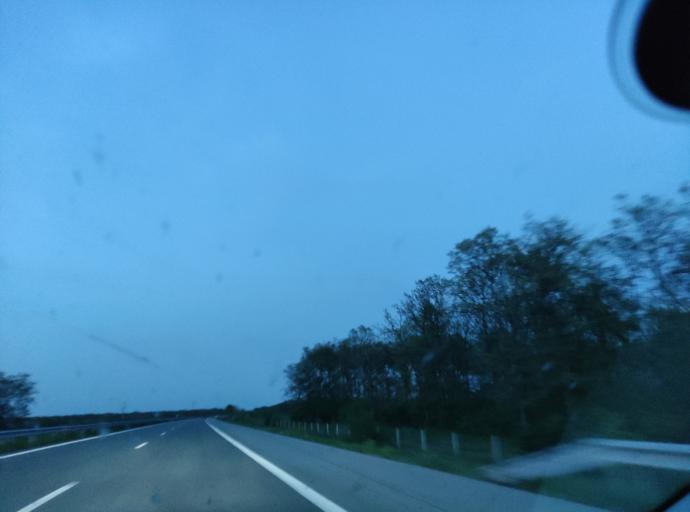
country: BG
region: Stara Zagora
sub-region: Obshtina Stara Zagora
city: Stara Zagora
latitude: 42.3576
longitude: 25.7493
